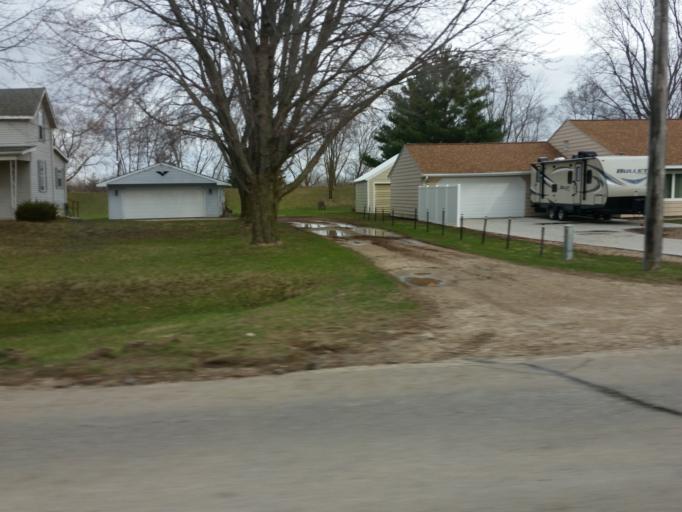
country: US
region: Iowa
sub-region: Black Hawk County
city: Elk Run Heights
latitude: 42.4727
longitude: -92.2193
